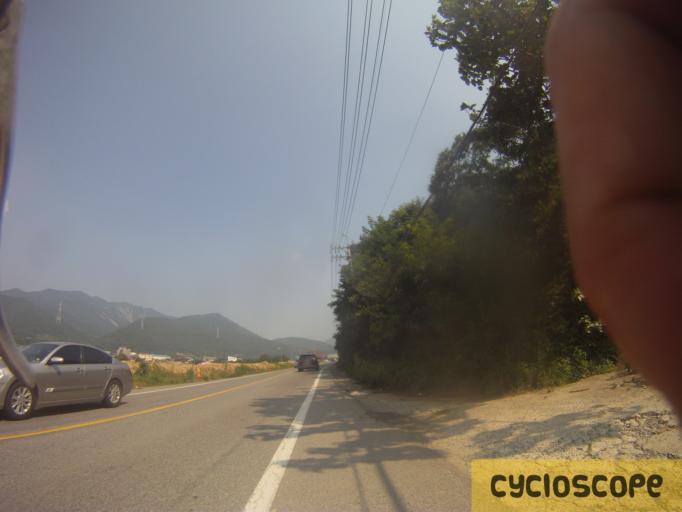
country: KR
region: Gyeongsangnam-do
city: Goseong
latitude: 34.8374
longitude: 128.0052
